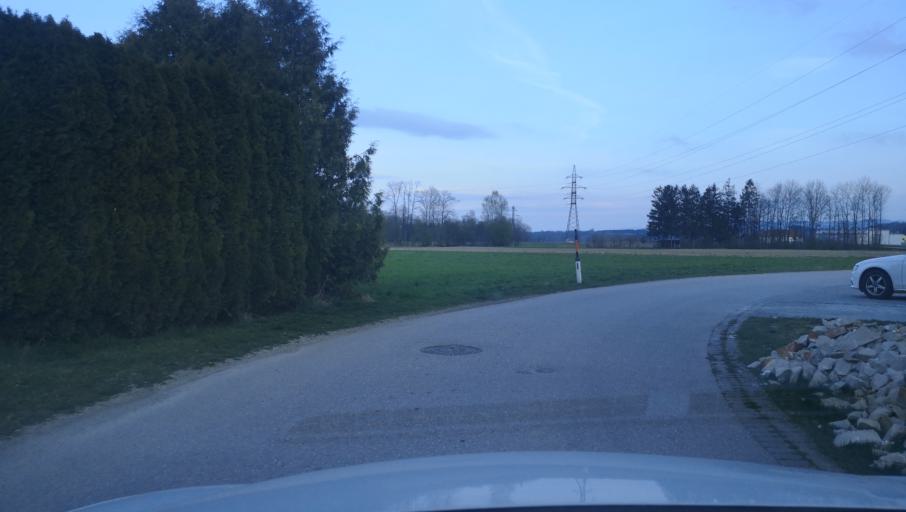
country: AT
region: Lower Austria
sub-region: Politischer Bezirk Amstetten
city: Amstetten
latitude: 48.1045
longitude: 14.9027
